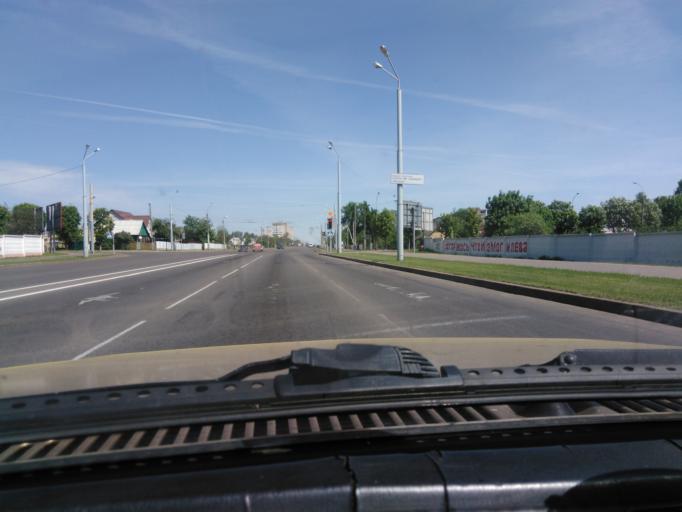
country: BY
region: Mogilev
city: Mahilyow
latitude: 53.9267
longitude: 30.3504
